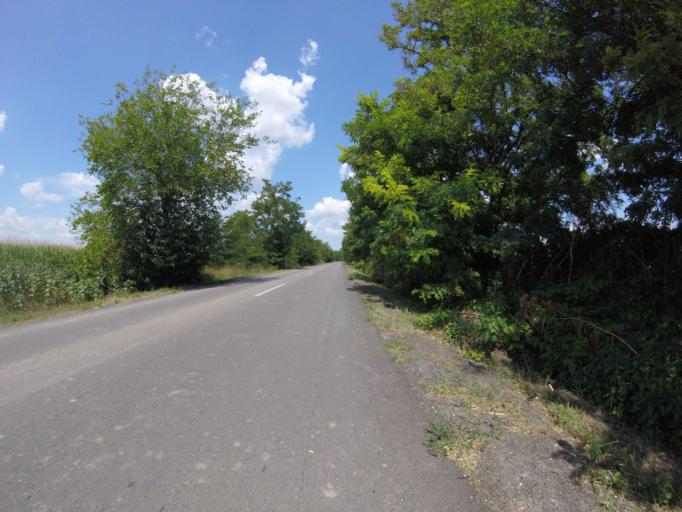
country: HU
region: Fejer
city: Adony
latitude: 47.1262
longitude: 18.8975
